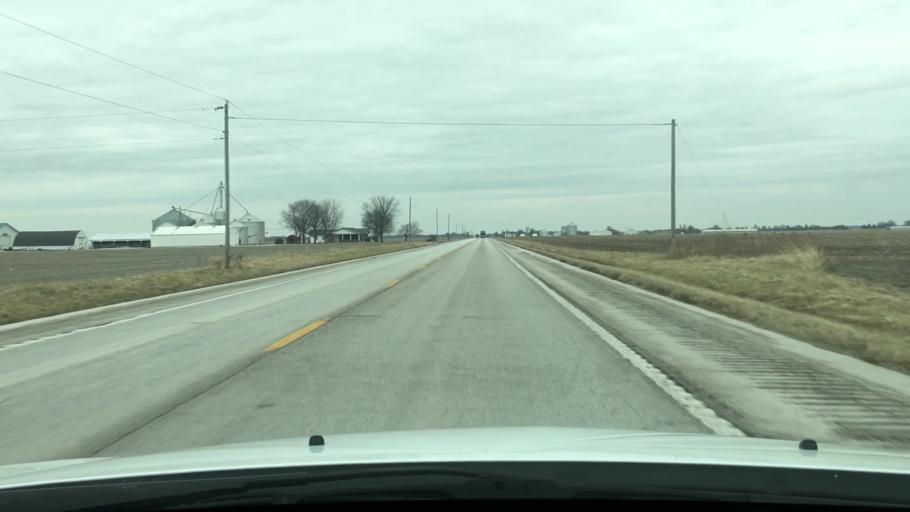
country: US
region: Missouri
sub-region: Audrain County
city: Vandalia
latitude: 39.2679
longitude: -91.6446
